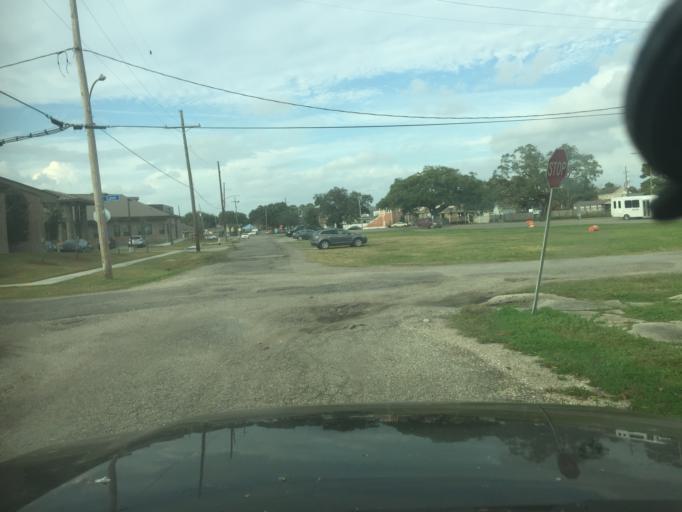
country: US
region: Louisiana
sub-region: Orleans Parish
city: New Orleans
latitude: 29.9975
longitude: -90.0807
